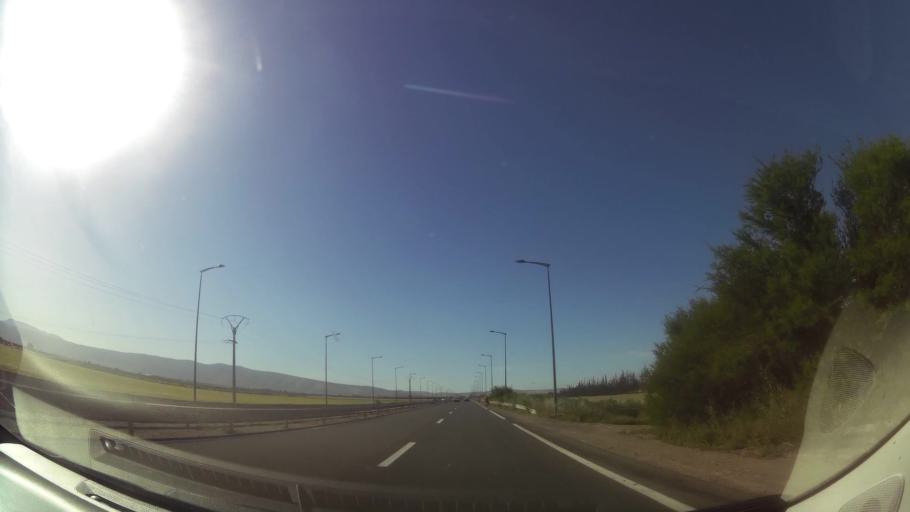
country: MA
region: Oriental
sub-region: Oujda-Angad
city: Oujda
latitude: 34.8300
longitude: -1.9740
